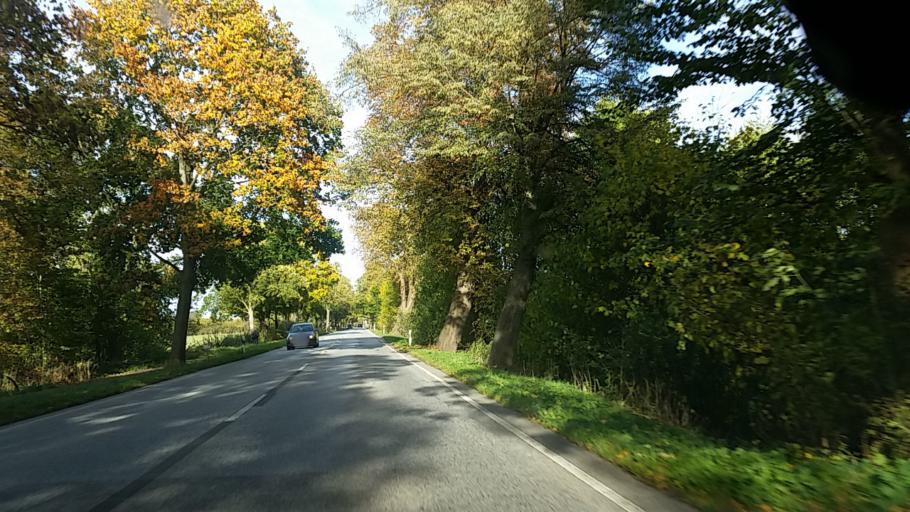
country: DE
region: Schleswig-Holstein
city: Delingsdorf
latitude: 53.6980
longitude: 10.2445
